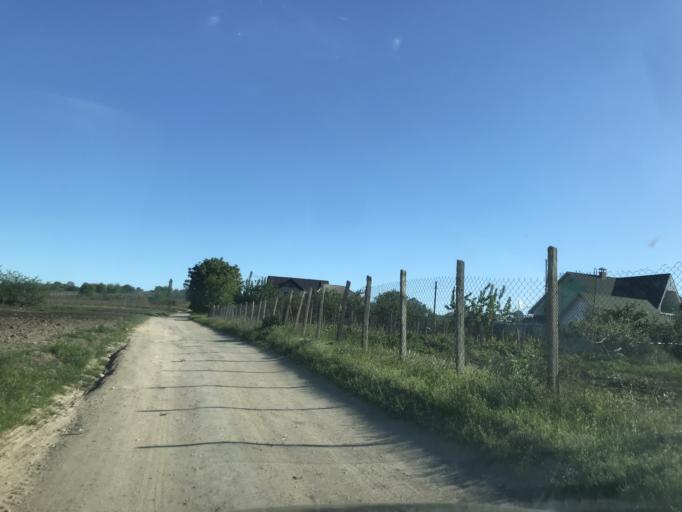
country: MD
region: Chisinau
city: Cricova
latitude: 47.2356
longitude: 28.8154
